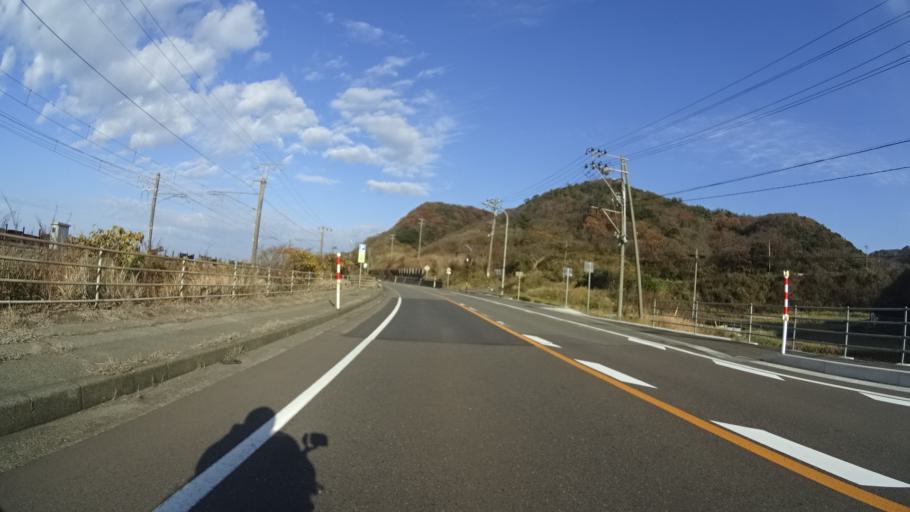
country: JP
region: Niigata
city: Kashiwazaki
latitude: 37.2974
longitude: 138.4089
